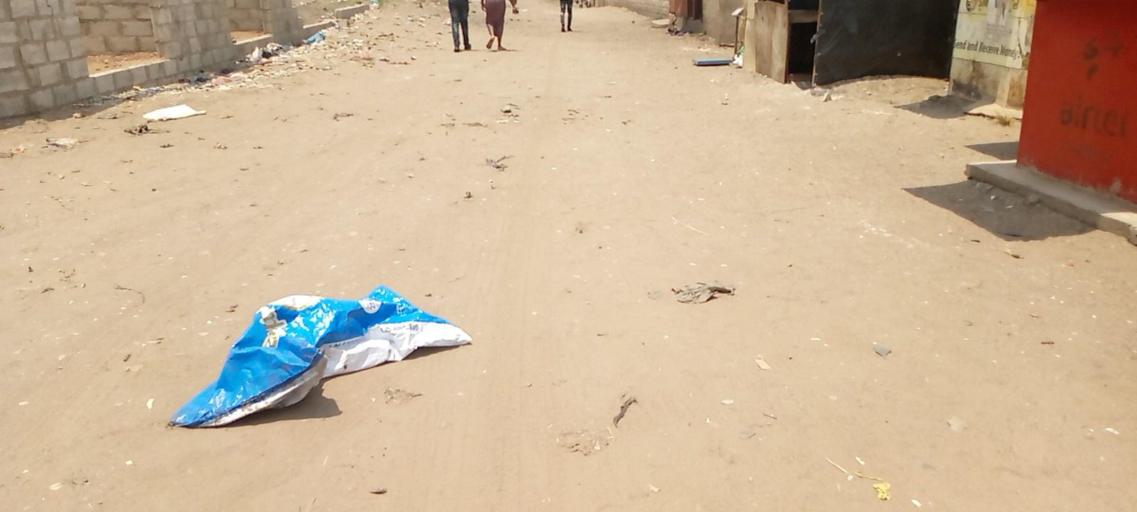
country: ZM
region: Lusaka
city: Lusaka
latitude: -15.4008
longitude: 28.3490
